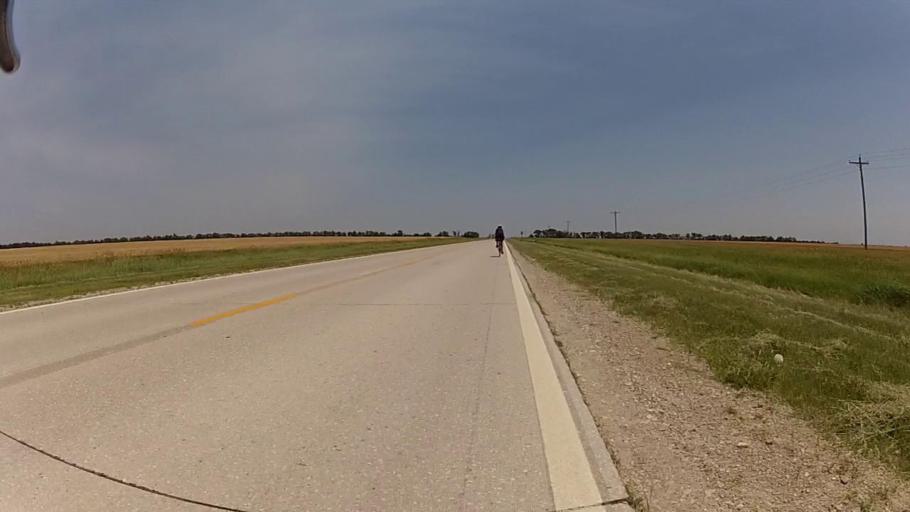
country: US
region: Kansas
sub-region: Sumner County
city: Wellington
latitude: 37.0574
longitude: -97.2713
